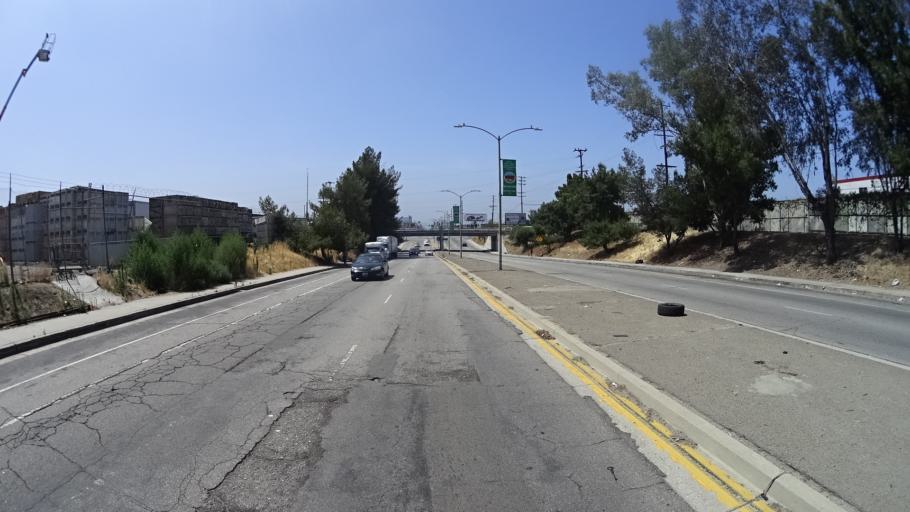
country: US
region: California
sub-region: Los Angeles County
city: North Hollywood
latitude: 34.2025
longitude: -118.3965
